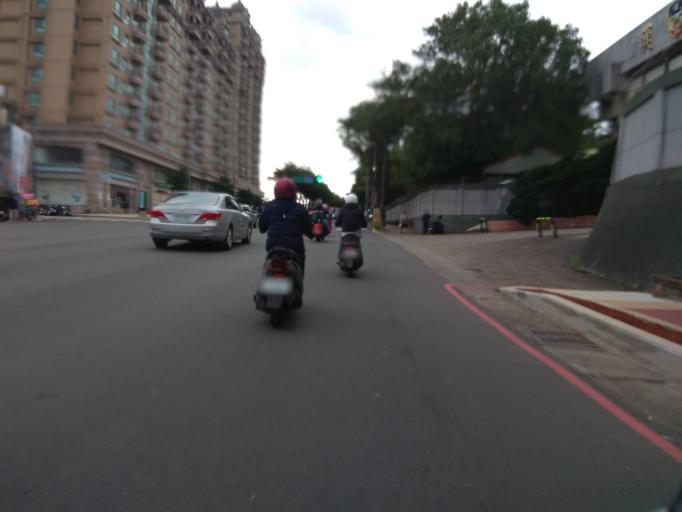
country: TW
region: Taiwan
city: Daxi
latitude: 24.9047
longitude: 121.2116
